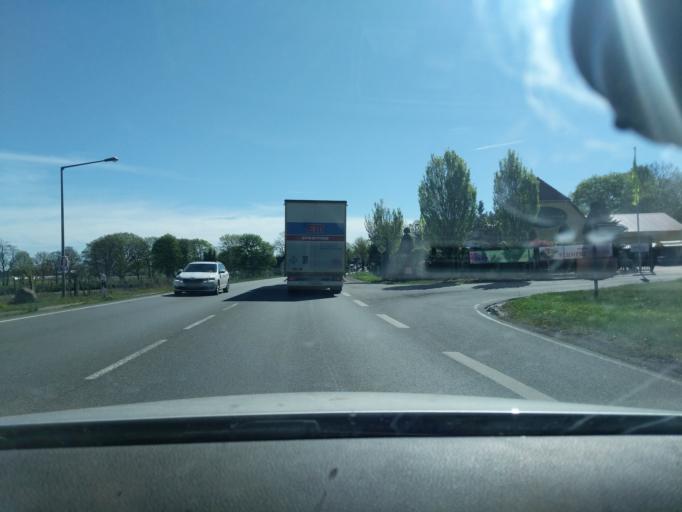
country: DE
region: Lower Saxony
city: Buxtehude
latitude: 53.4540
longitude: 9.7347
